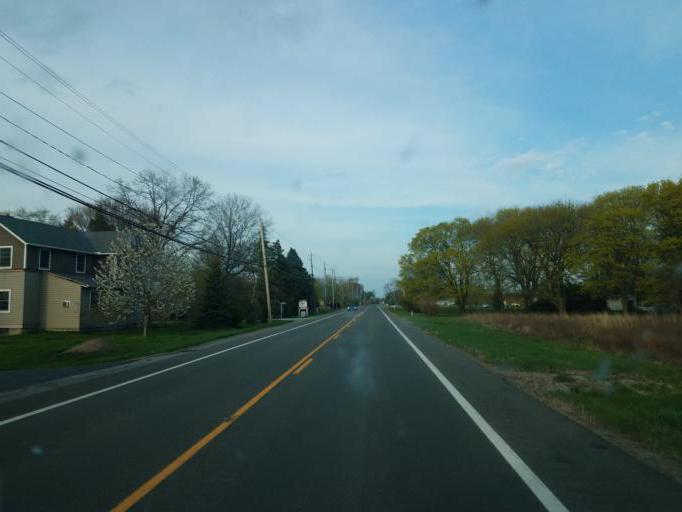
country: US
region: Ohio
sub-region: Lorain County
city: Vermilion
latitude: 41.4131
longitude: -82.3949
